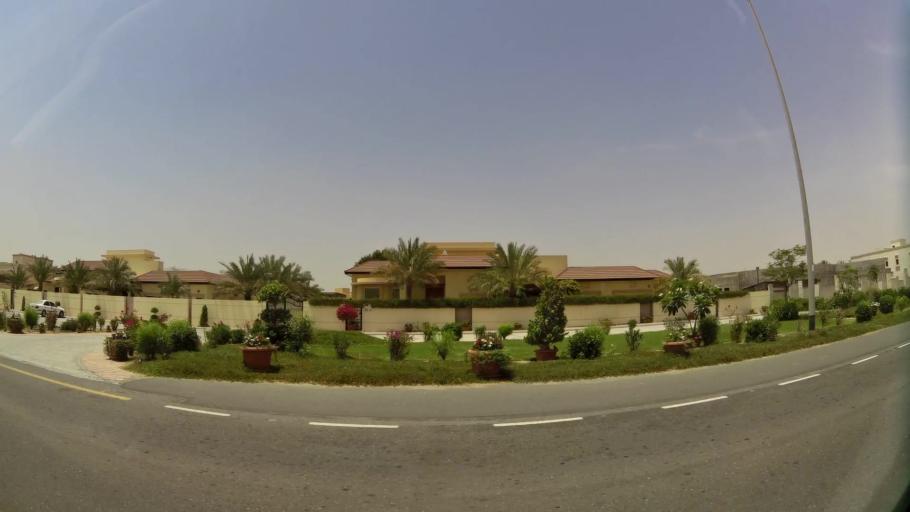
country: AE
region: Ash Shariqah
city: Sharjah
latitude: 25.2351
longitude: 55.4785
